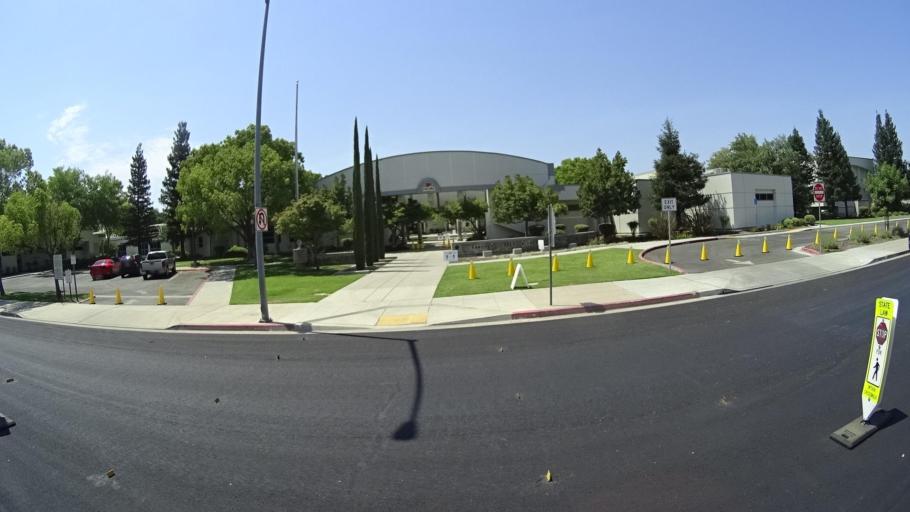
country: US
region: California
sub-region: Fresno County
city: Sunnyside
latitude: 36.7436
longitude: -119.6847
